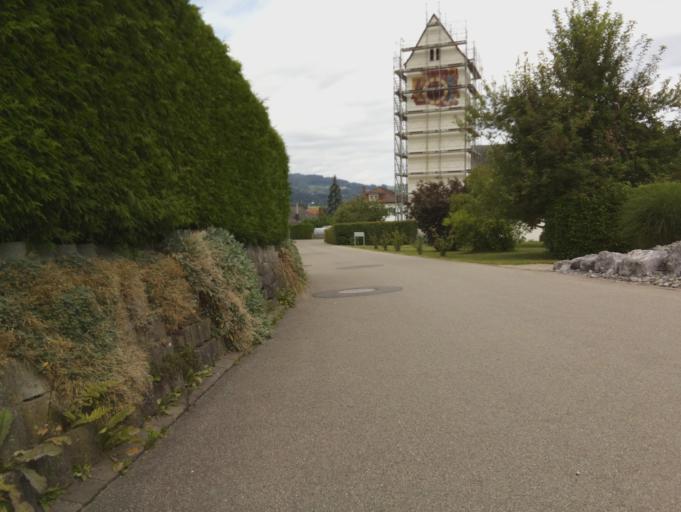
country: CH
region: Saint Gallen
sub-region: Wahlkreis Toggenburg
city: Ganterschwil
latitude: 47.3809
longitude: 9.0936
